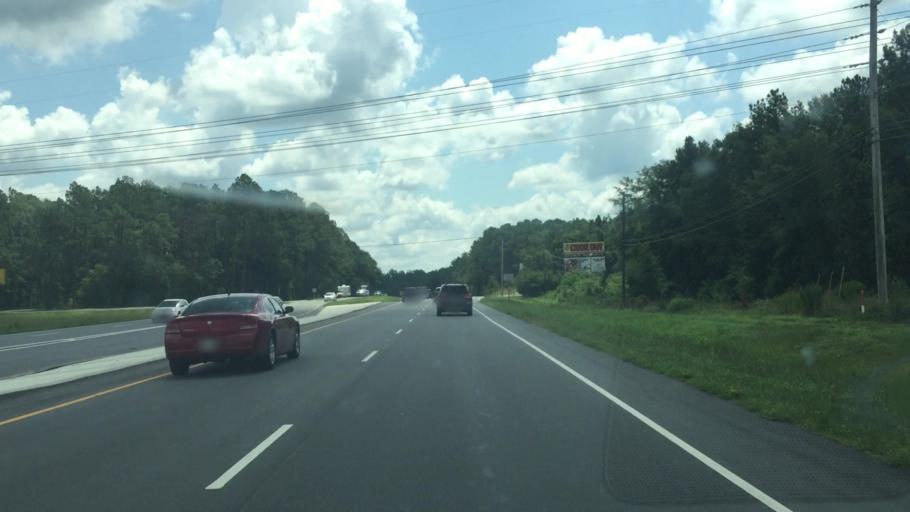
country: US
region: North Carolina
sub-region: Scotland County
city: Laurel Hill
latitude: 34.8029
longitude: -79.5389
